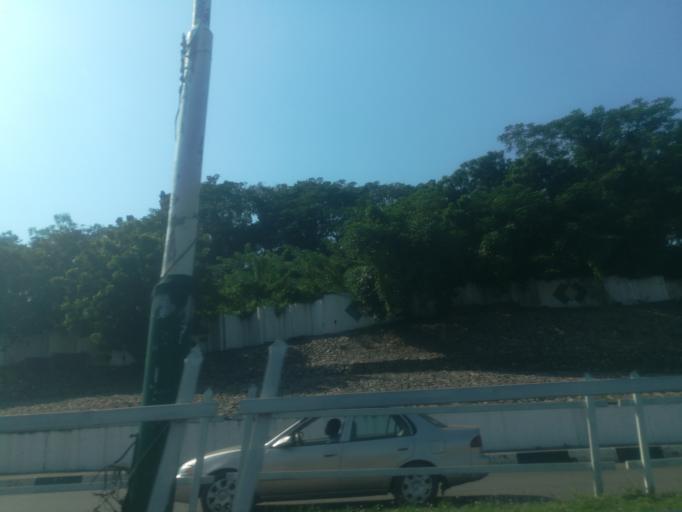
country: NG
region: Ogun
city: Abeokuta
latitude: 7.1431
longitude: 3.3415
